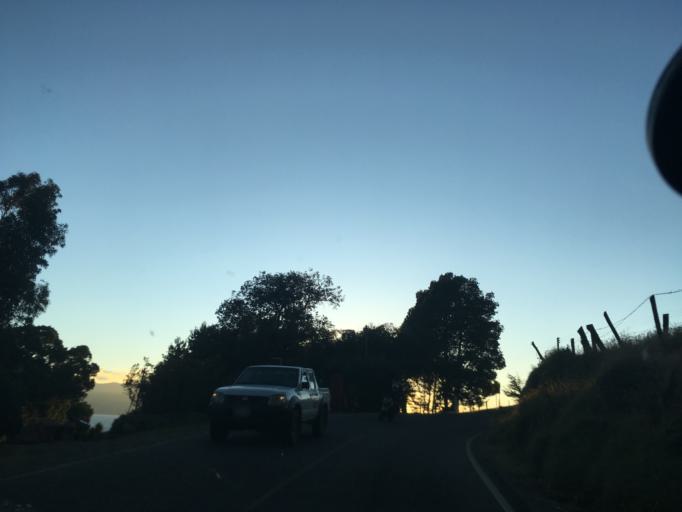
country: CO
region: Boyaca
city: Aquitania
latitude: 5.5617
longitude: -72.8827
